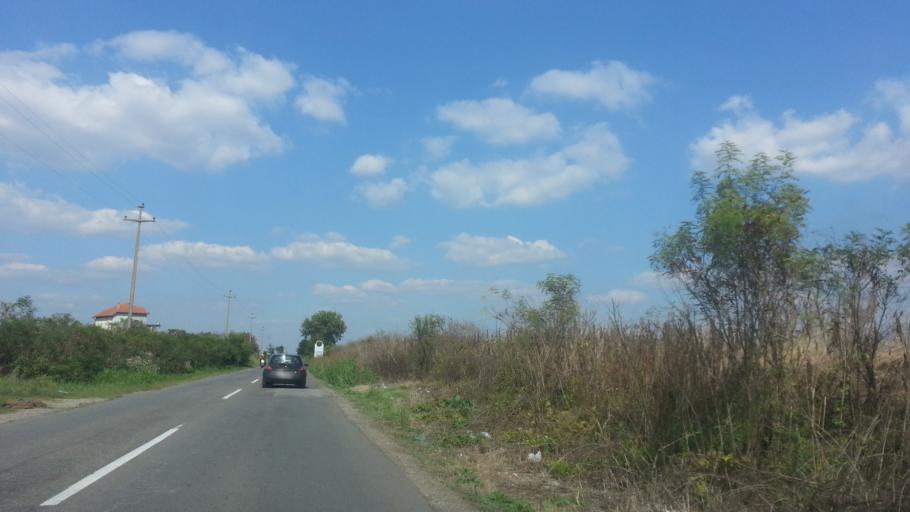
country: RS
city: Novi Banovci
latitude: 44.9313
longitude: 20.2800
